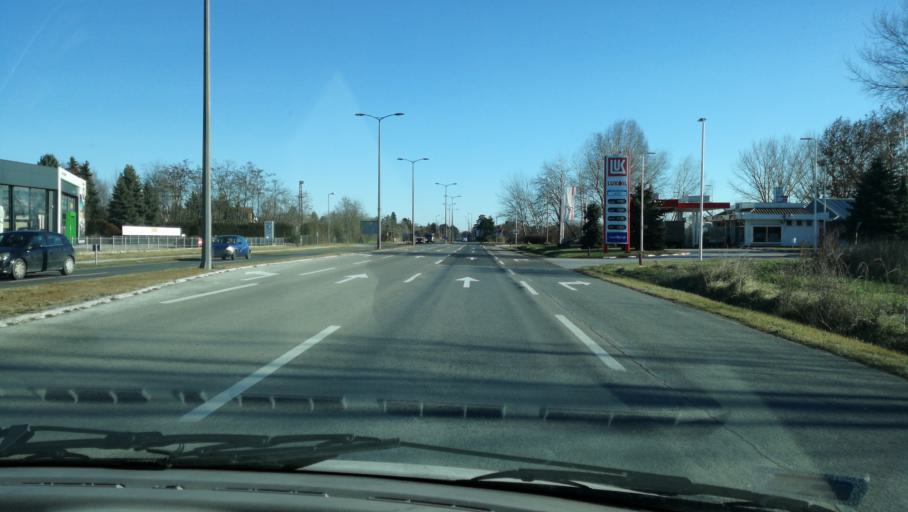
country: RS
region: Autonomna Pokrajina Vojvodina
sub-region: Severnobacki Okrug
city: Subotica
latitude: 46.1040
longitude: 19.7395
